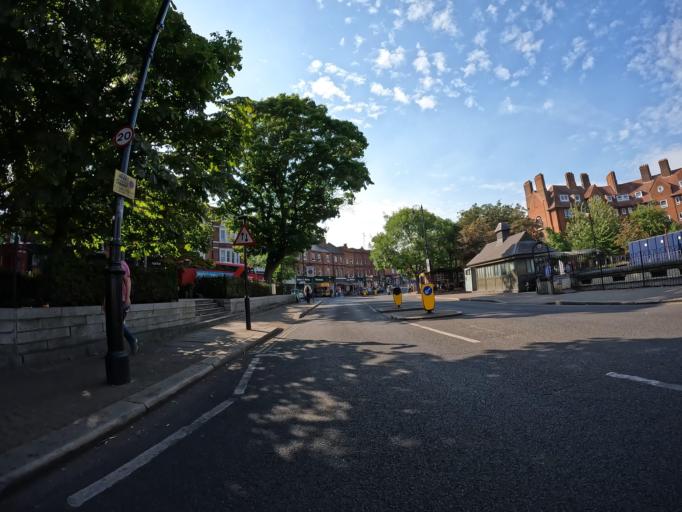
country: GB
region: England
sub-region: Greater London
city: Hendon
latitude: 51.6096
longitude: -0.2196
